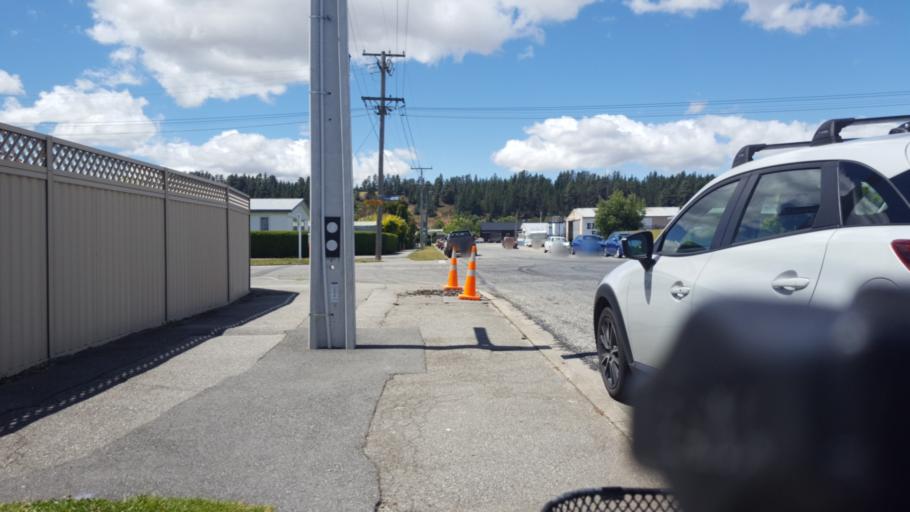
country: NZ
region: Otago
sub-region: Queenstown-Lakes District
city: Wanaka
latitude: -45.2446
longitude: 169.3899
